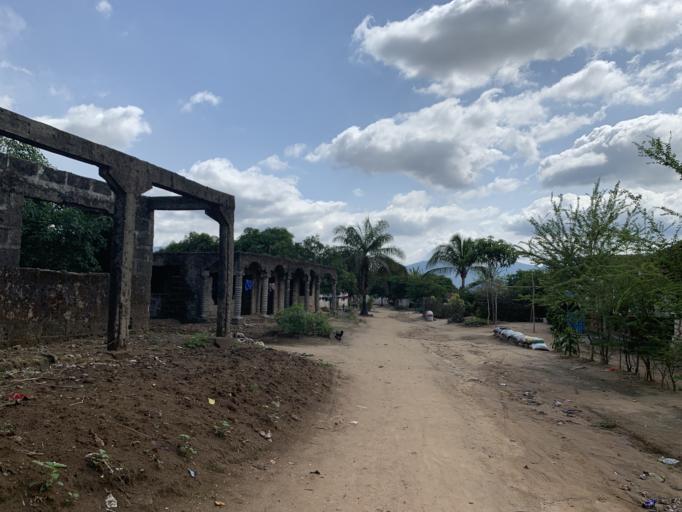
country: SL
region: Western Area
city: Waterloo
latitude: 8.3353
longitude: -13.0502
